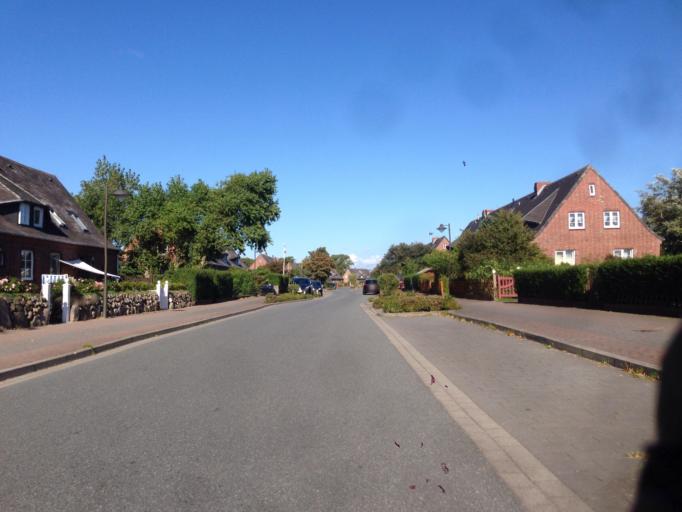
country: DE
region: Schleswig-Holstein
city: List
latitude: 55.0194
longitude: 8.4230
